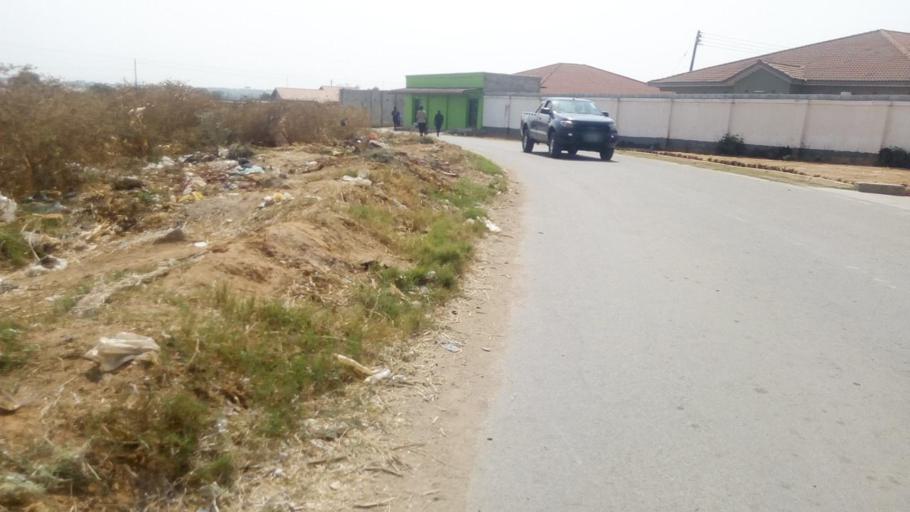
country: ZM
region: Lusaka
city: Lusaka
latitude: -15.3602
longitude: 28.2841
